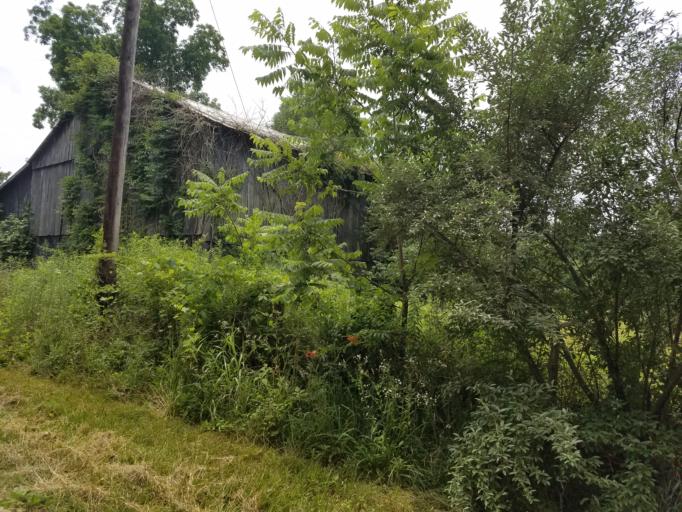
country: US
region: Kentucky
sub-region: Edmonson County
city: Brownsville
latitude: 37.3489
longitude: -86.1068
